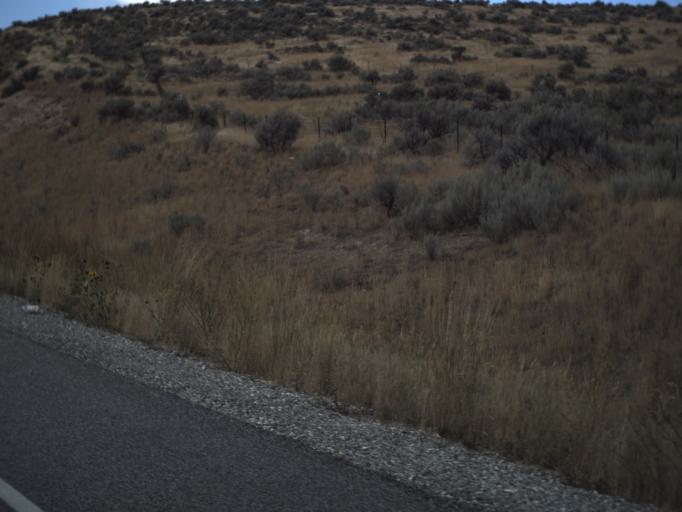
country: US
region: Utah
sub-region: Box Elder County
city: Garland
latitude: 41.8970
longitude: -112.5476
